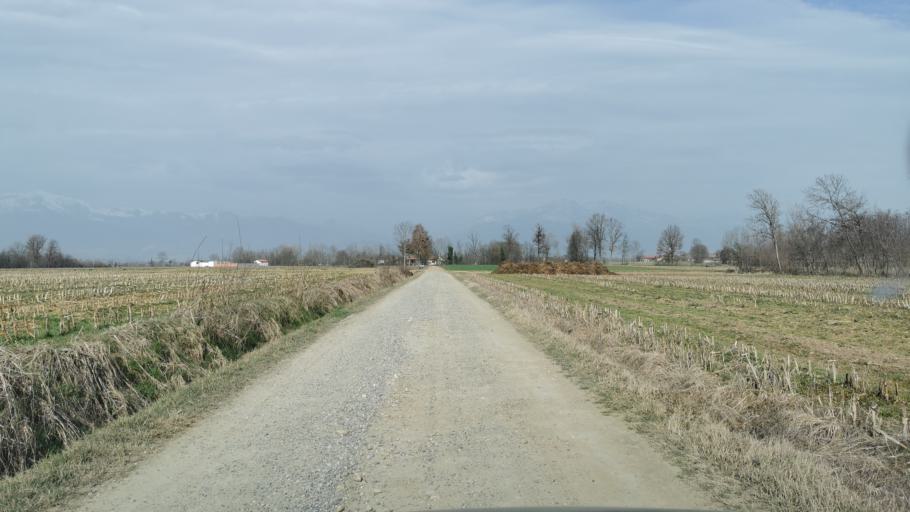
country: IT
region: Piedmont
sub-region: Provincia di Torino
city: Front
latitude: 45.2801
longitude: 7.6987
